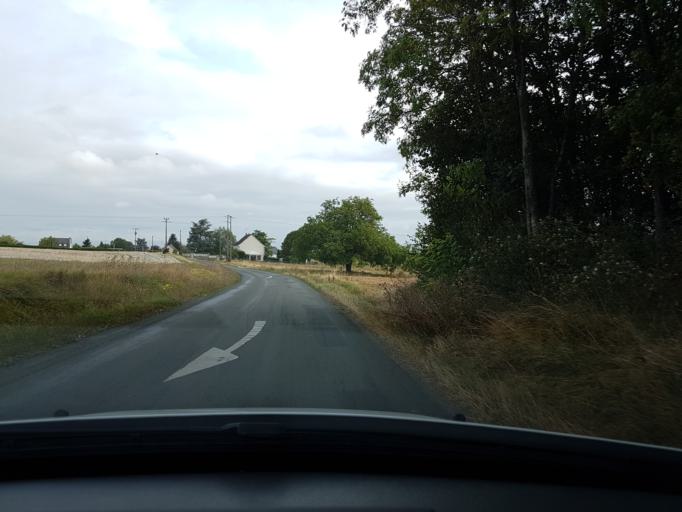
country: FR
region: Centre
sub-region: Departement d'Indre-et-Loire
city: Azay-sur-Cher
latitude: 47.3414
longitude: 0.8323
